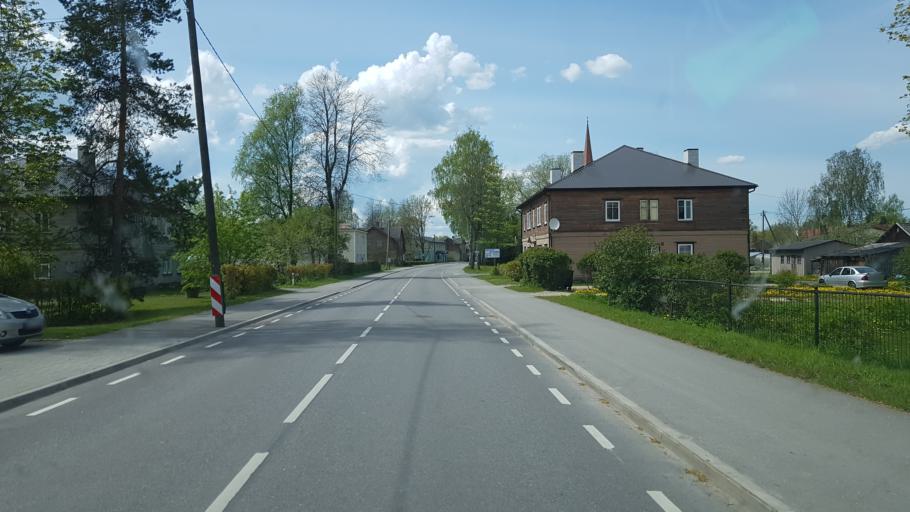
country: EE
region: Jogevamaa
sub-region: Mustvee linn
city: Mustvee
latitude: 58.8484
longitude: 26.9377
